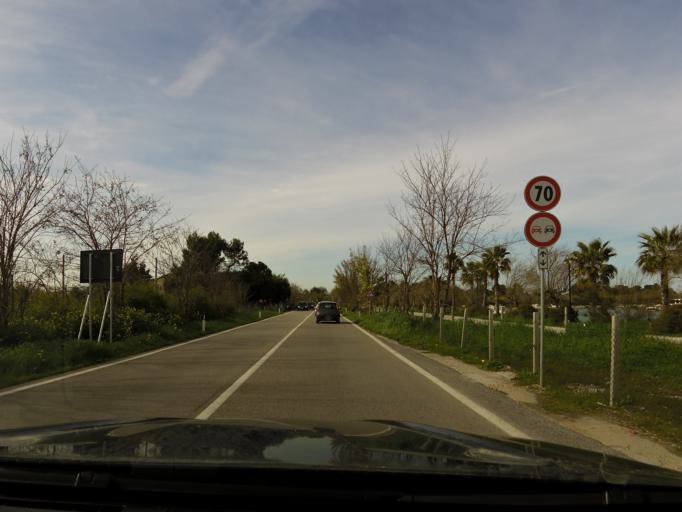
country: IT
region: The Marches
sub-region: Provincia di Macerata
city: Porto Potenza Picena
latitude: 43.3923
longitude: 13.6814
